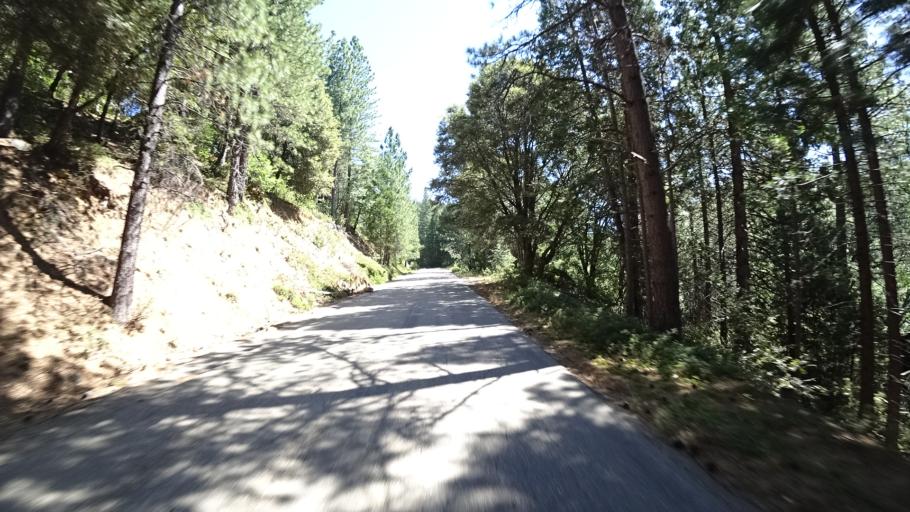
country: US
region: California
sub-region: Amador County
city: Pioneer
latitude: 38.4259
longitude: -120.4825
